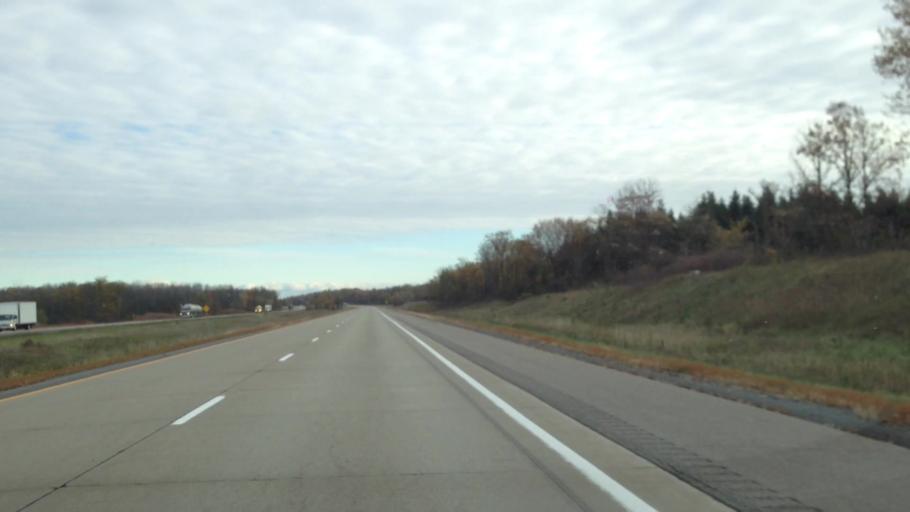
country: CA
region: Ontario
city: Hawkesbury
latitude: 45.3855
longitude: -74.7936
